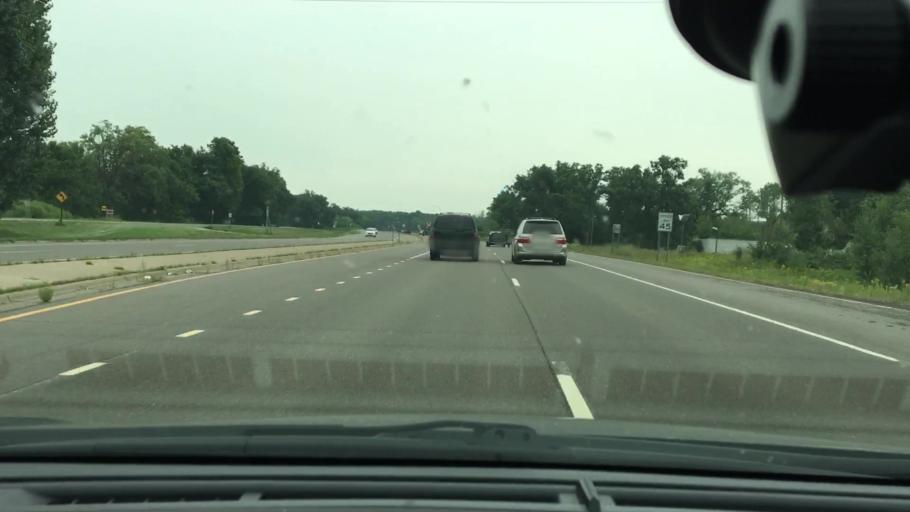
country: US
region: Minnesota
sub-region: Mille Lacs County
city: Vineland
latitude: 46.1917
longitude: -93.7612
